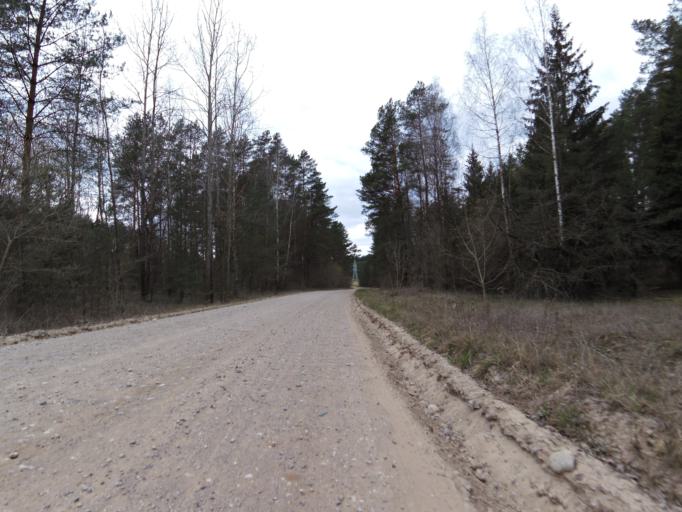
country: LT
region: Vilnius County
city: Pilaite
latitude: 54.6773
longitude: 25.1770
